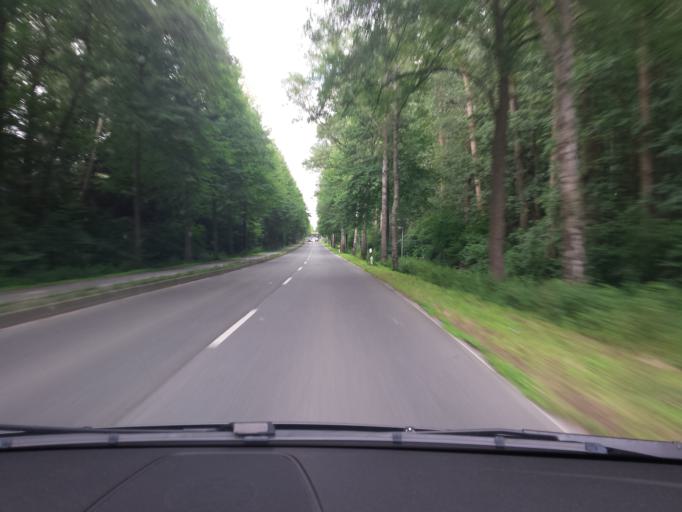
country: DE
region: North Rhine-Westphalia
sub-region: Regierungsbezirk Arnsberg
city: Lippstadt
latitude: 51.6990
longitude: 8.3584
